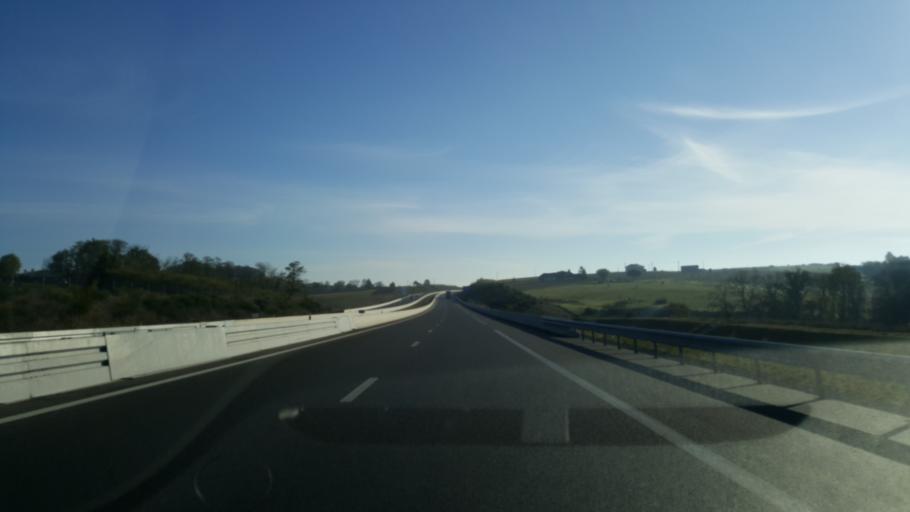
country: FR
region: Rhone-Alpes
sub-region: Departement du Rhone
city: Bully
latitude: 45.8685
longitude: 4.5643
